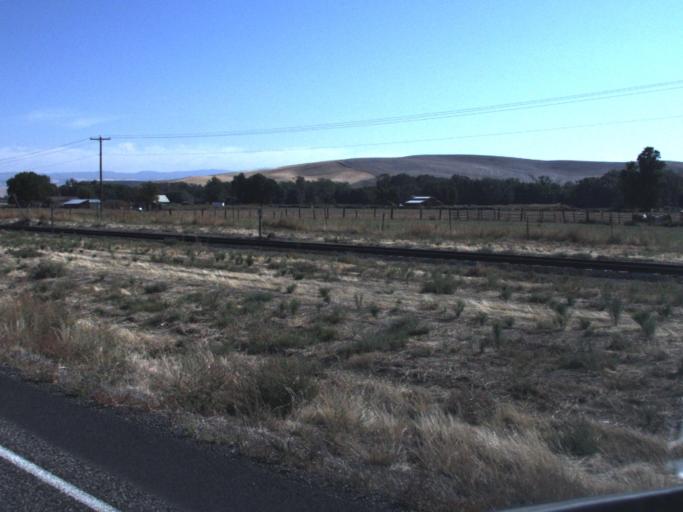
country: US
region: Washington
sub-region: Walla Walla County
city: Waitsburg
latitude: 46.2996
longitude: -118.2992
